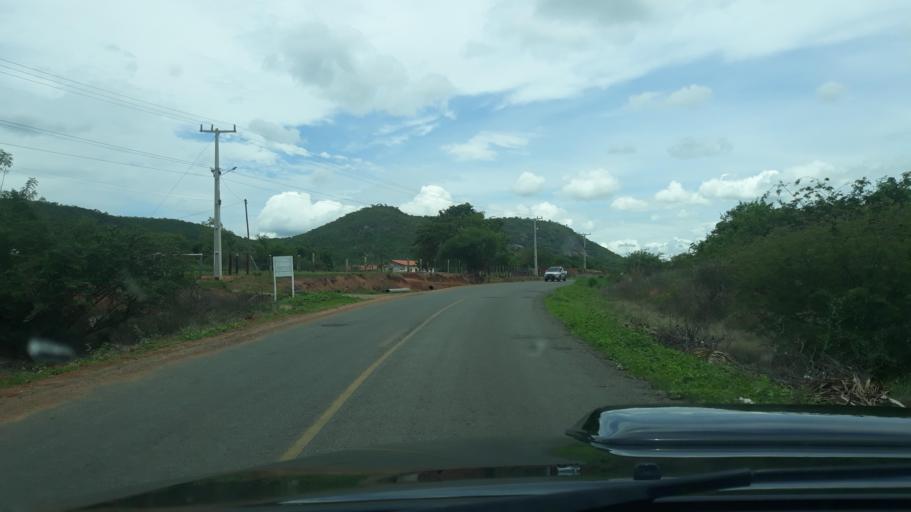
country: BR
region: Bahia
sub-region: Guanambi
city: Guanambi
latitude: -14.1181
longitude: -42.8550
